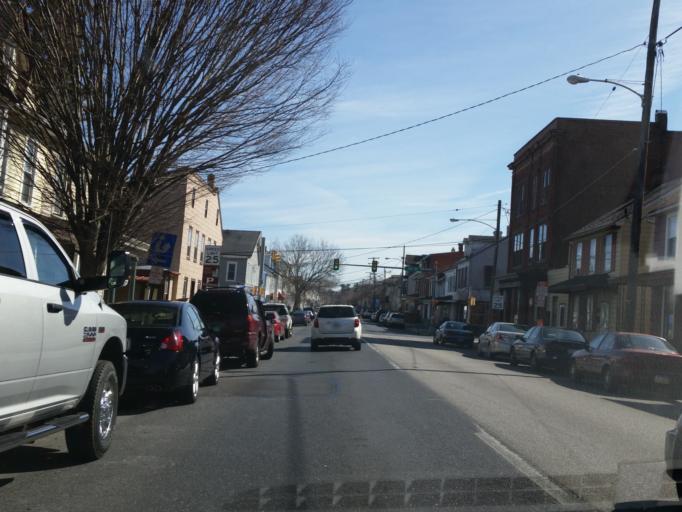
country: US
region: Pennsylvania
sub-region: Lebanon County
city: Lebanon
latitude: 40.3369
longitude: -76.4216
